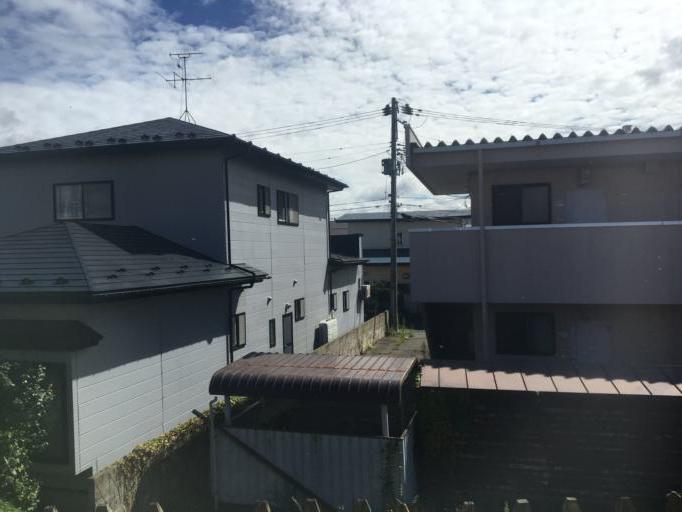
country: JP
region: Akita
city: Akita
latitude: 39.6962
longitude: 140.1173
